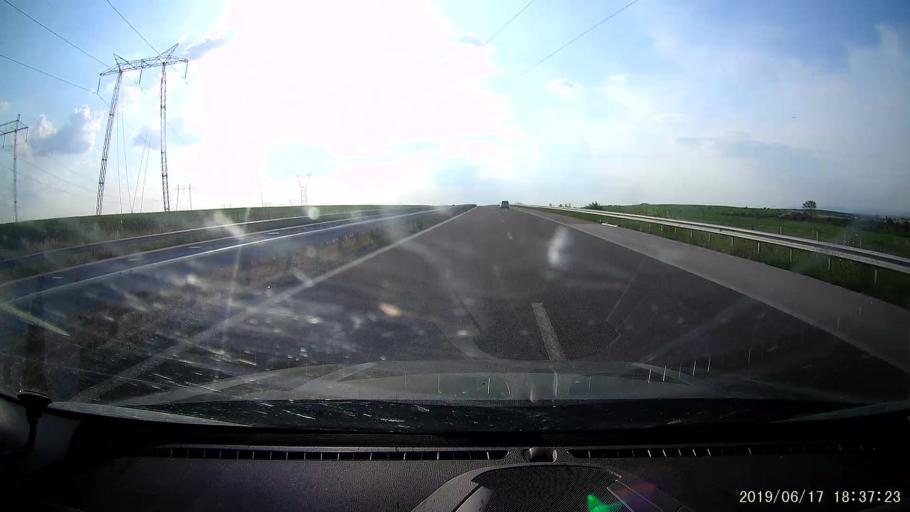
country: BG
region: Stara Zagora
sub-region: Obshtina Chirpan
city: Chirpan
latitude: 42.1297
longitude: 25.3622
